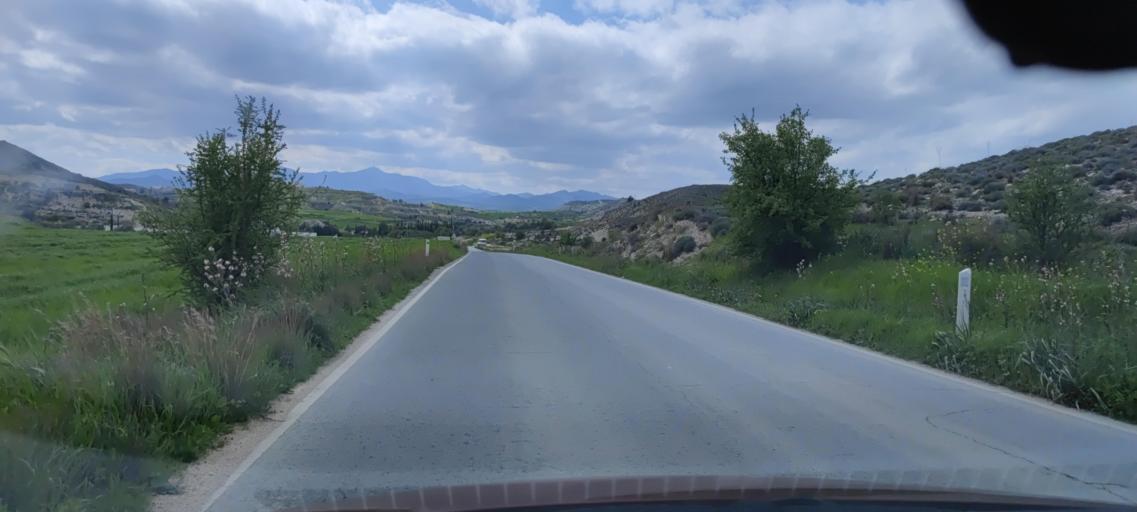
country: CY
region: Lefkosia
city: Tseri
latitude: 35.0297
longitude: 33.3077
